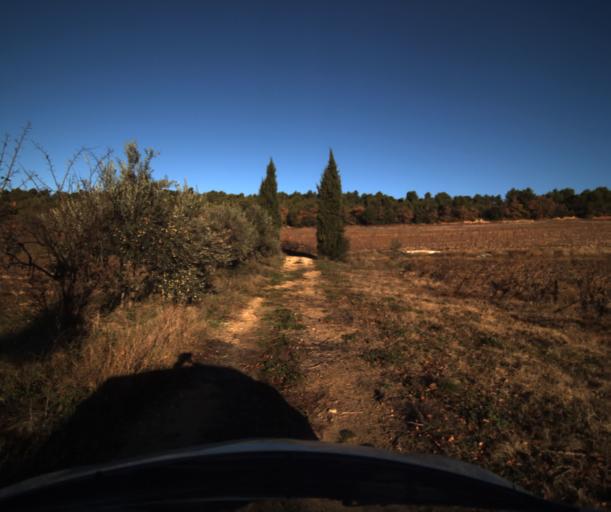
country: FR
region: Provence-Alpes-Cote d'Azur
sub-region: Departement du Vaucluse
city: Ansouis
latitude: 43.7234
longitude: 5.4849
